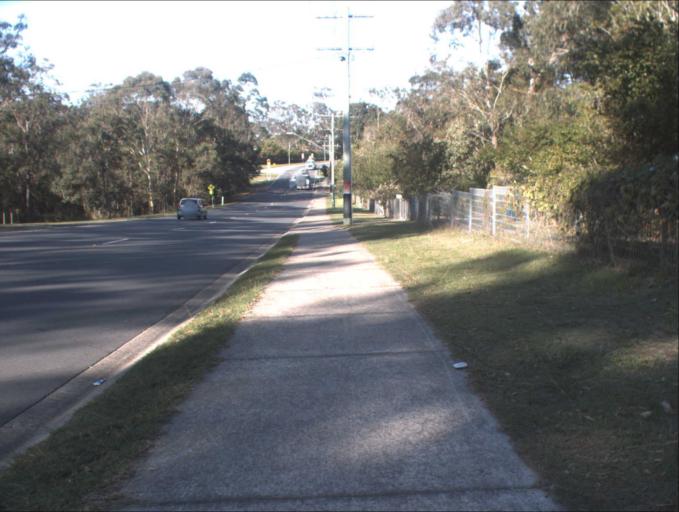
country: AU
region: Queensland
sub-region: Logan
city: Park Ridge South
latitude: -27.6995
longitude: 153.0303
